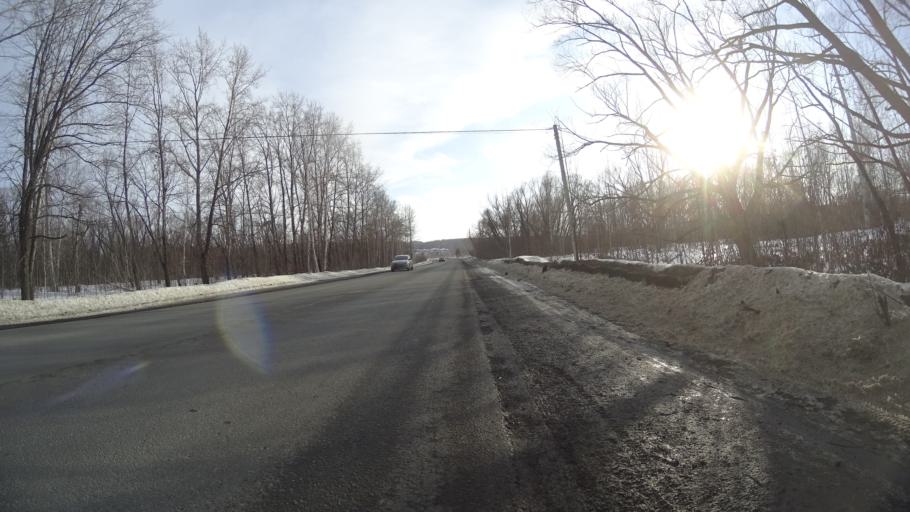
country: RU
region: Chelyabinsk
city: Sargazy
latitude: 55.1420
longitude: 61.2828
